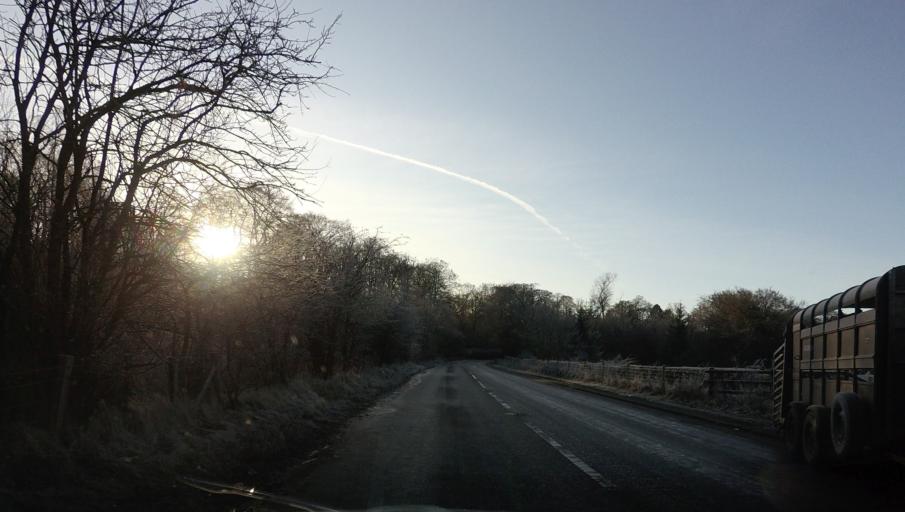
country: GB
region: Scotland
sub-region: North Lanarkshire
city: Newmains
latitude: 55.7973
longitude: -3.8504
